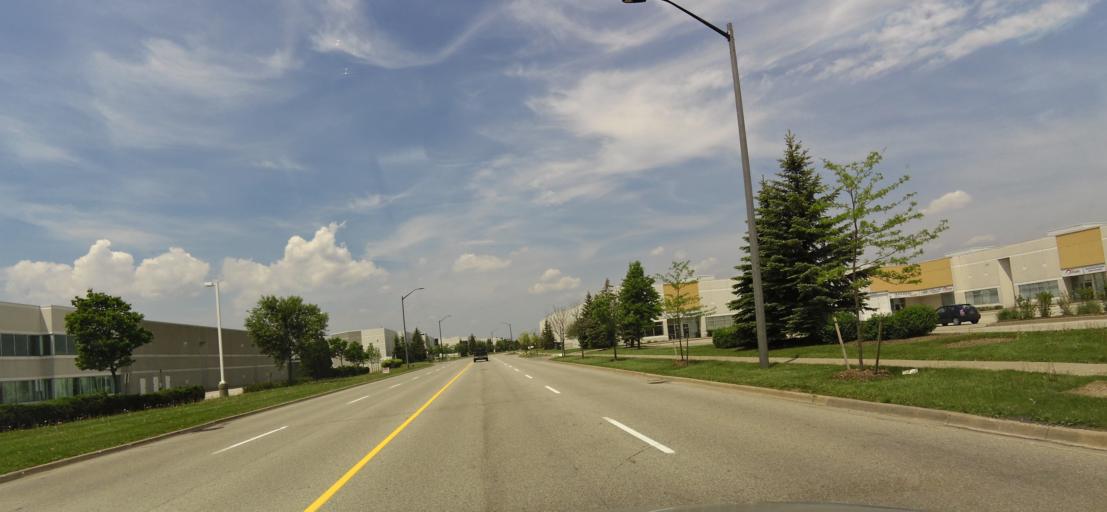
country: CA
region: Ontario
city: Oakville
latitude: 43.5167
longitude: -79.6980
